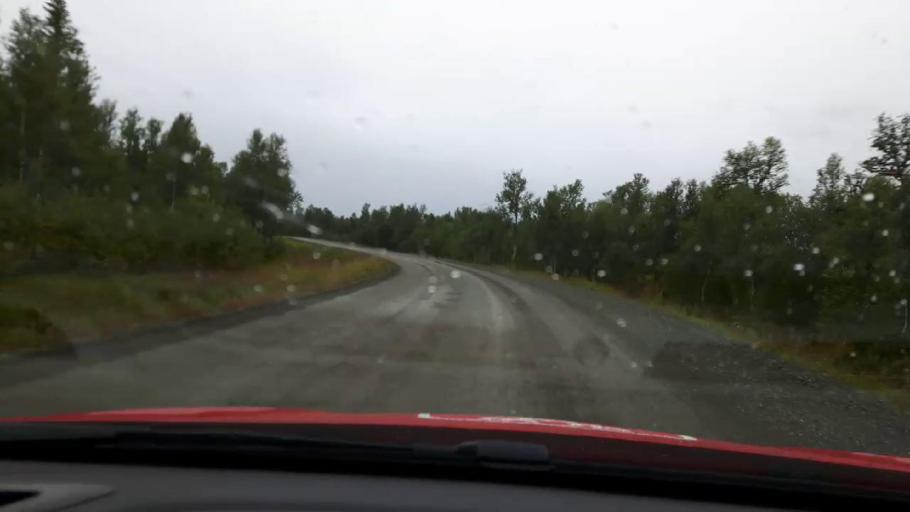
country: NO
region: Nord-Trondelag
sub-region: Meraker
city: Meraker
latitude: 63.5828
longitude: 12.2673
